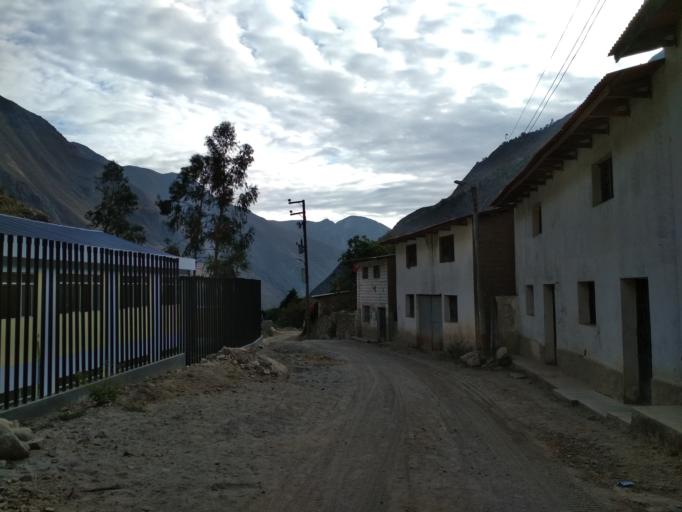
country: PE
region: Lima
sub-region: Provincia de Yauyos
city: Cacra
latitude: -12.8227
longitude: -75.7928
